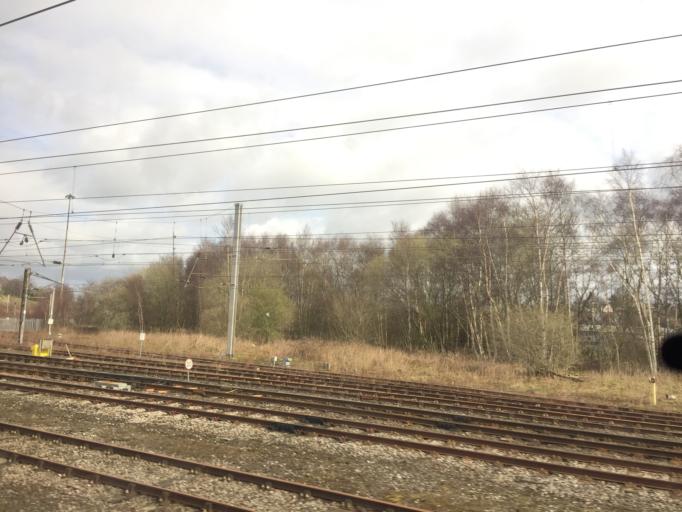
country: GB
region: England
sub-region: Cumbria
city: Carlisle
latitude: 54.8789
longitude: -2.9196
